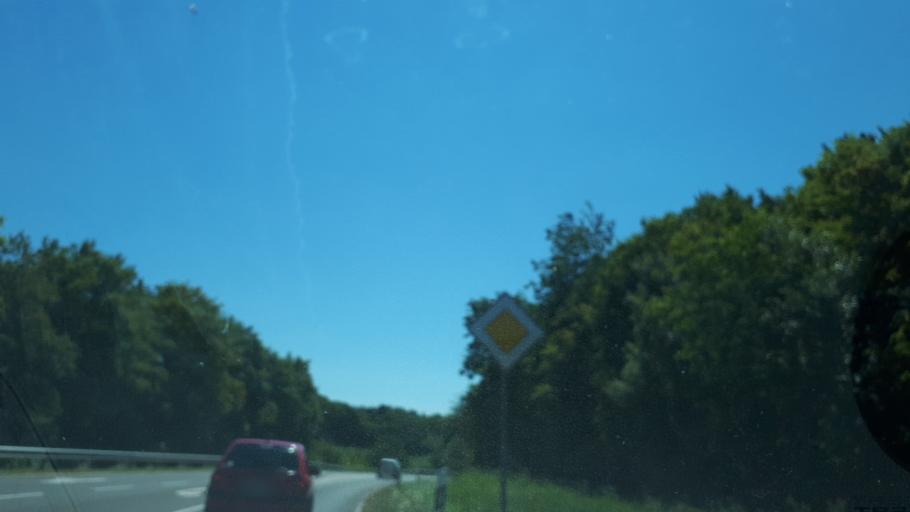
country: DE
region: Rheinland-Pfalz
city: Landkern
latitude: 50.1832
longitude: 7.1605
